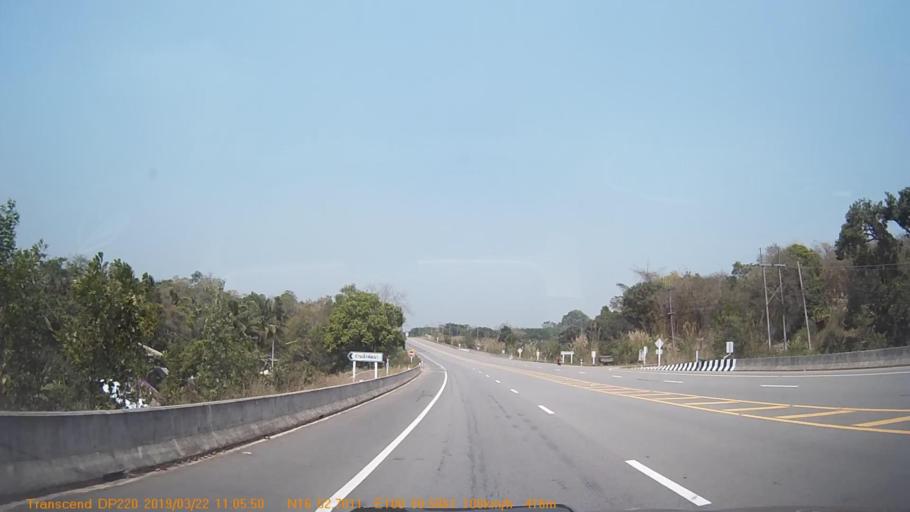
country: TH
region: Phitsanulok
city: Nakhon Thai
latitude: 16.8786
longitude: 100.8427
